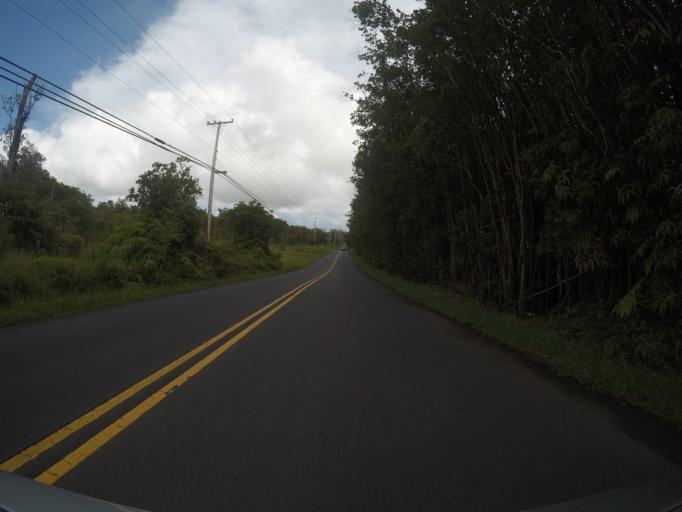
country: US
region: Hawaii
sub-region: Hawaii County
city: Fern Acres
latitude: 19.4815
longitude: -155.1454
